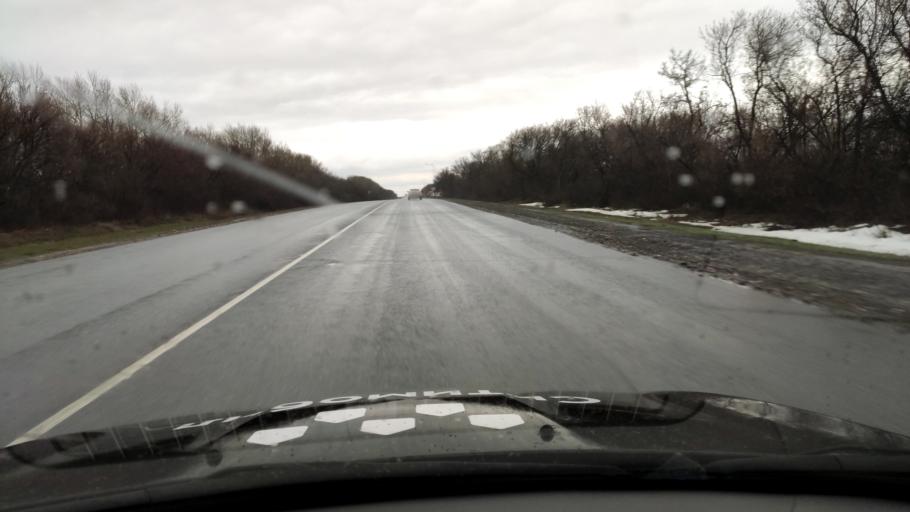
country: RU
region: Samara
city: Obsharovka
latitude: 53.2211
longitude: 48.7531
